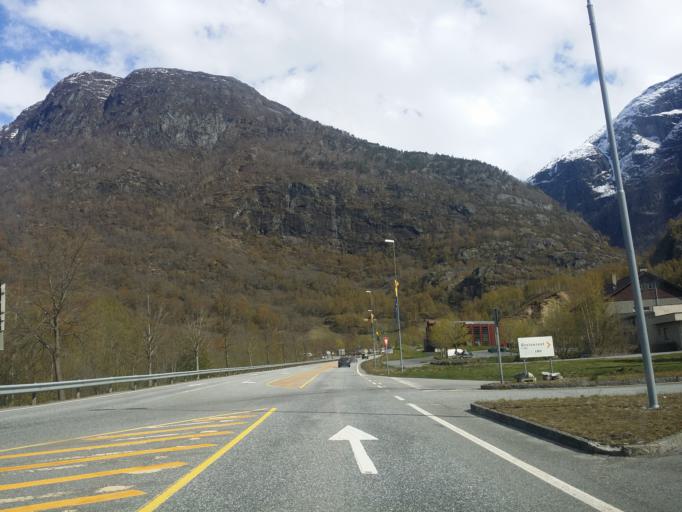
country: NO
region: Hordaland
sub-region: Eidfjord
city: Eidfjord
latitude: 60.4239
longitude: 7.1310
